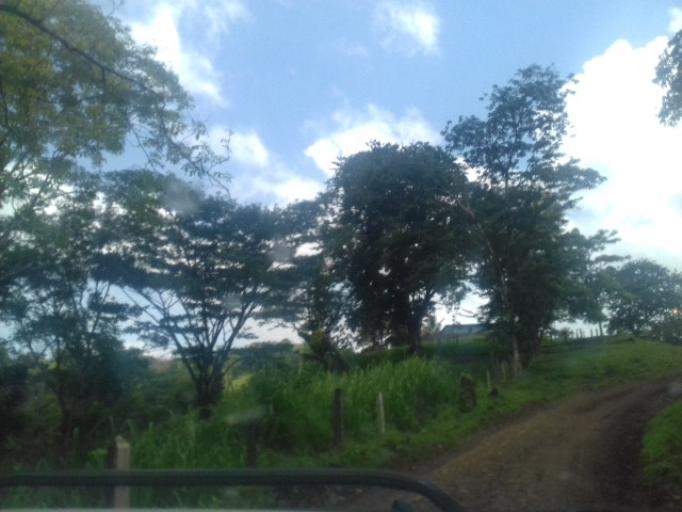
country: NI
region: Matagalpa
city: Matiguas
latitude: 12.9233
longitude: -85.3665
